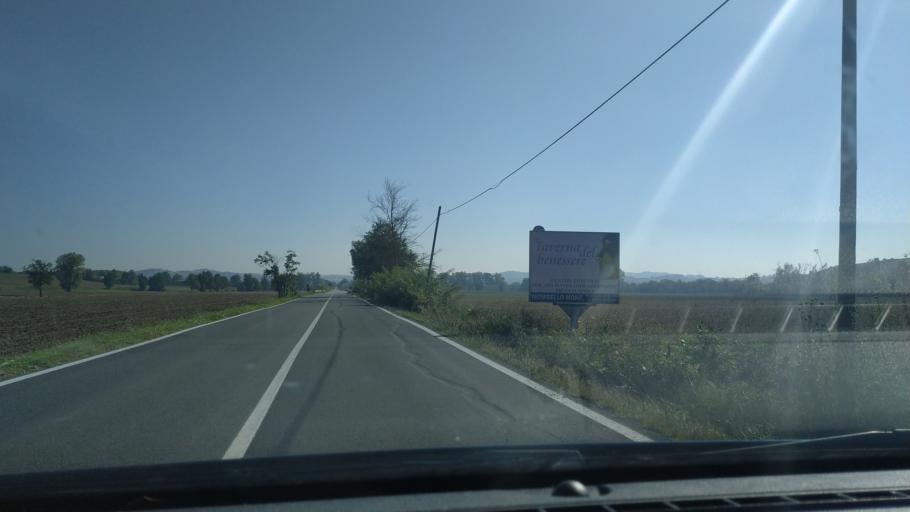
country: IT
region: Piedmont
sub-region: Provincia di Alessandria
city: Serralunga di Crea
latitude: 45.1132
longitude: 8.2874
